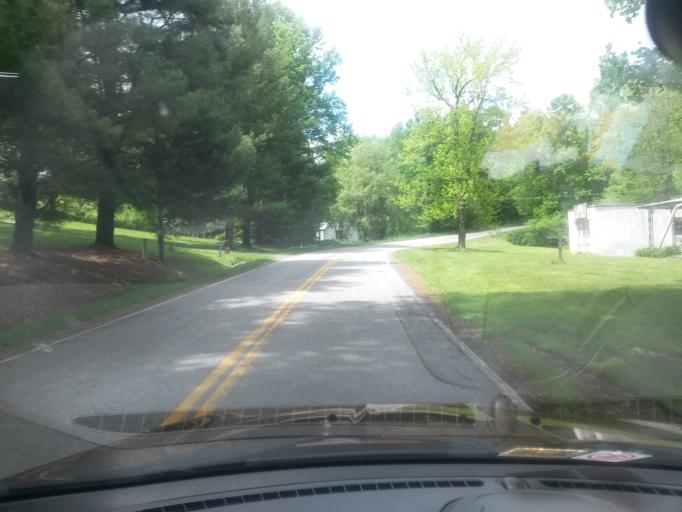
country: US
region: Virginia
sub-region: Patrick County
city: Stuart
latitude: 36.7427
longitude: -80.3902
